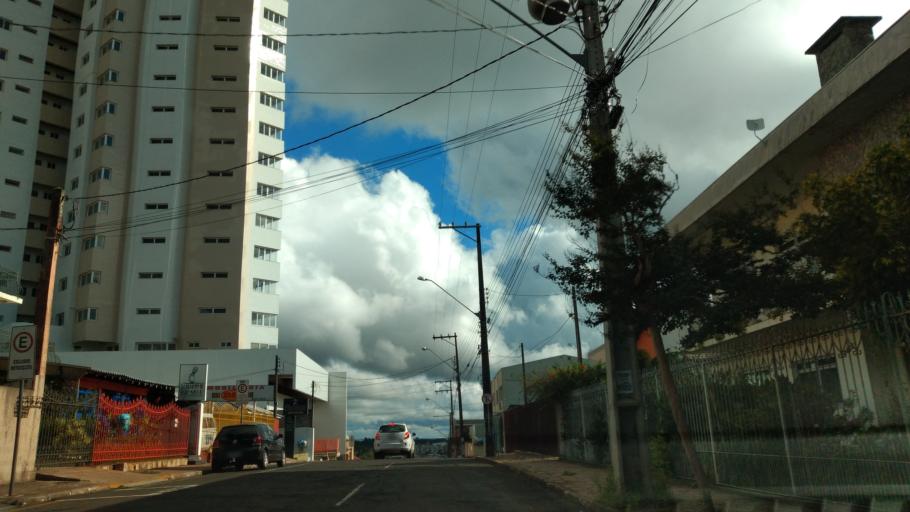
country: BR
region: Parana
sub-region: Guarapuava
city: Guarapuava
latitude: -25.3965
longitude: -51.4682
